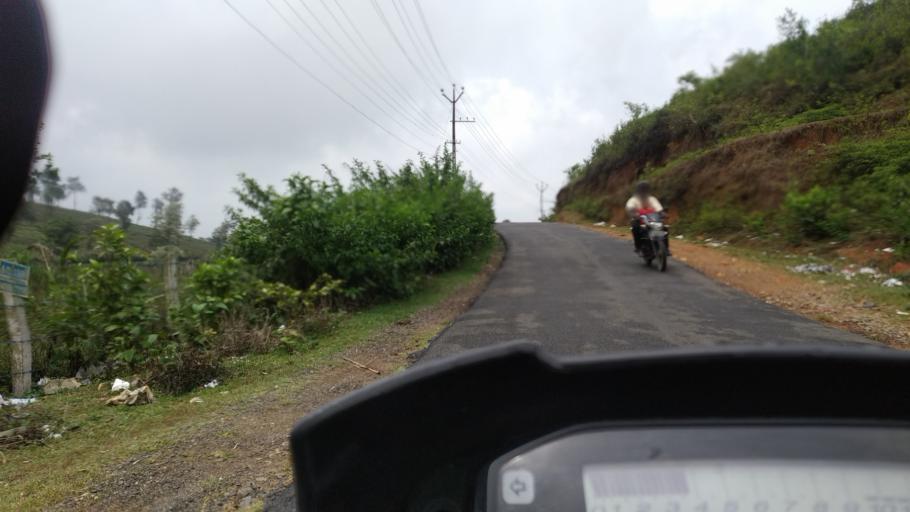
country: IN
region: Kerala
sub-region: Kottayam
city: Erattupetta
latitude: 9.6348
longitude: 76.9528
